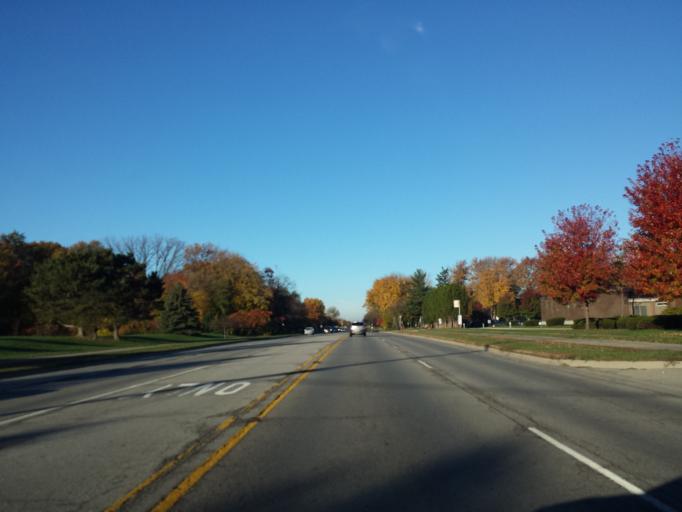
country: US
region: Michigan
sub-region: Oakland County
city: Bingham Farms
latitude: 42.5017
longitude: -83.2524
